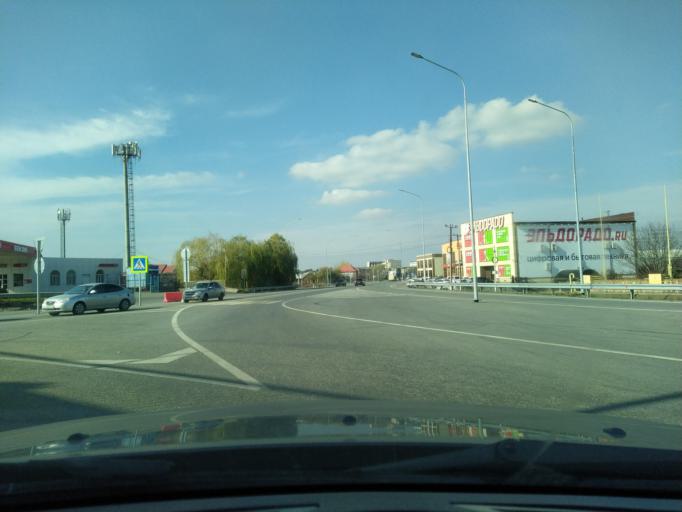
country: RU
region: Ingushetiya
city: Magas
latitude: 43.1954
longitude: 44.7611
